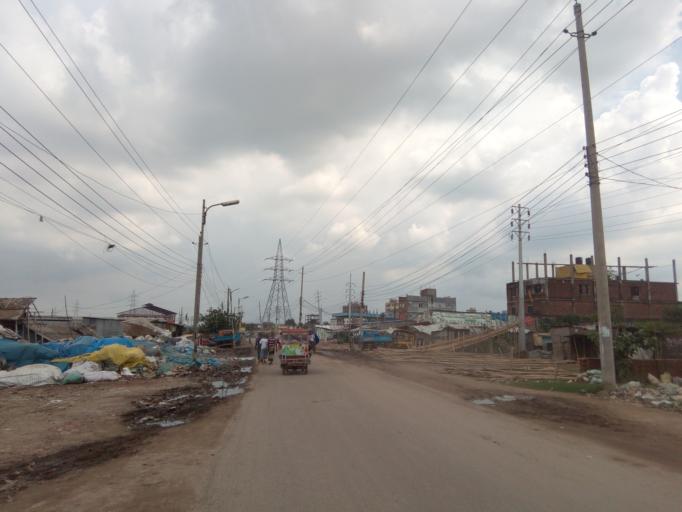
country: BD
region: Dhaka
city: Azimpur
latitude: 23.7341
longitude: 90.3622
